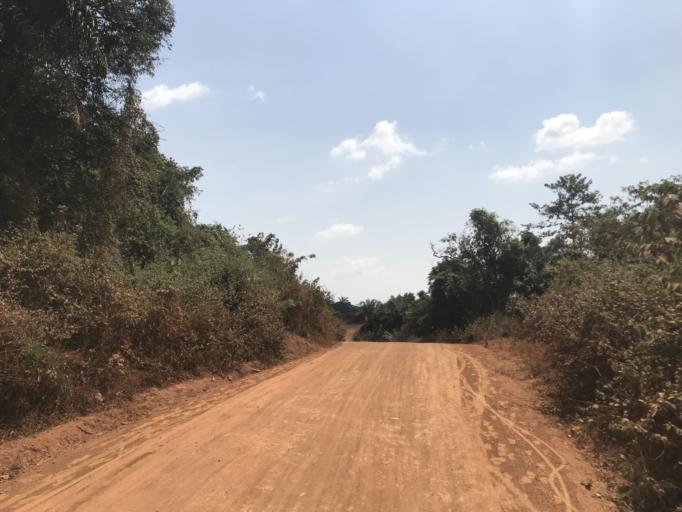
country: NG
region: Osun
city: Ifon
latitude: 7.8919
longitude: 4.4773
